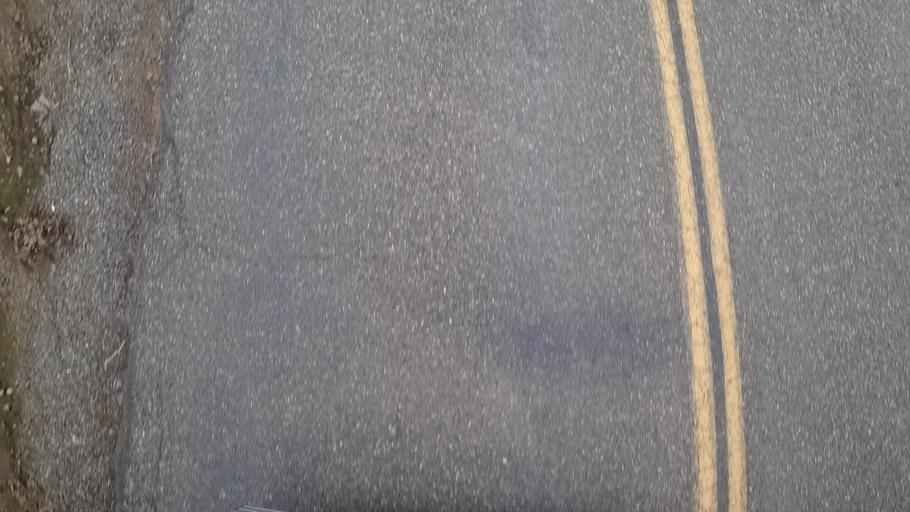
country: US
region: California
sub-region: Yuba County
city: Loma Rica
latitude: 39.3868
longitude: -121.4022
